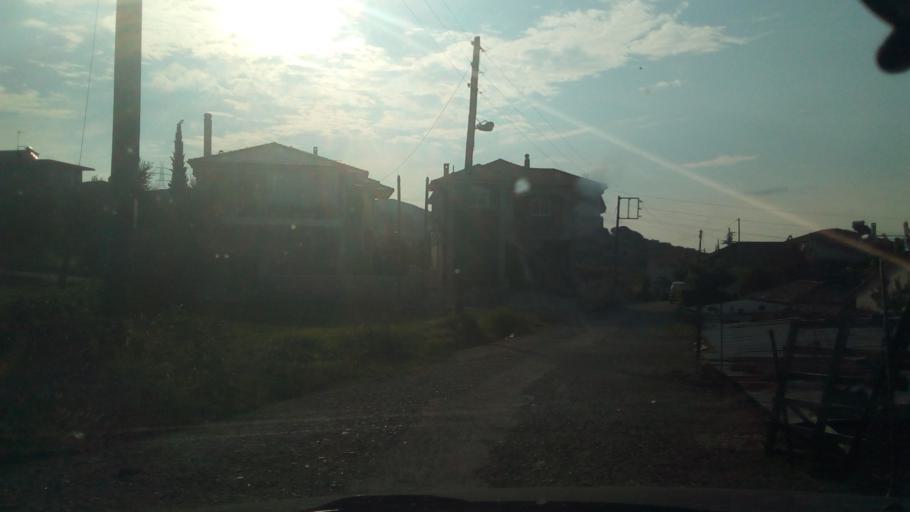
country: GR
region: West Greece
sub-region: Nomos Aitolias kai Akarnanias
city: Nafpaktos
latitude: 38.4163
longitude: 21.8947
